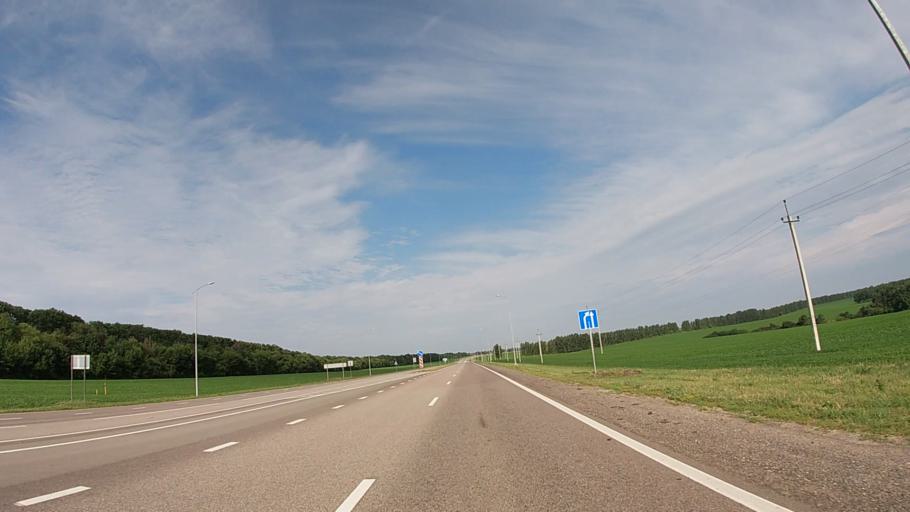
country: RU
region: Belgorod
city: Rakitnoye
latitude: 50.7905
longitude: 35.8855
